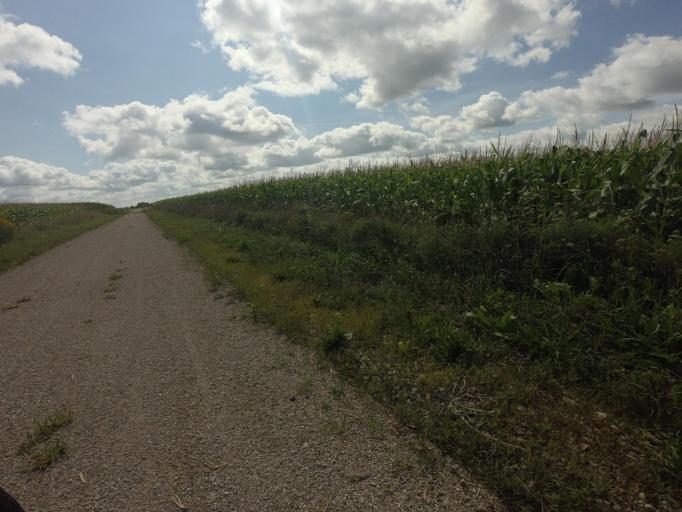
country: CA
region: Ontario
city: Huron East
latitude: 43.6443
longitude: -81.2131
